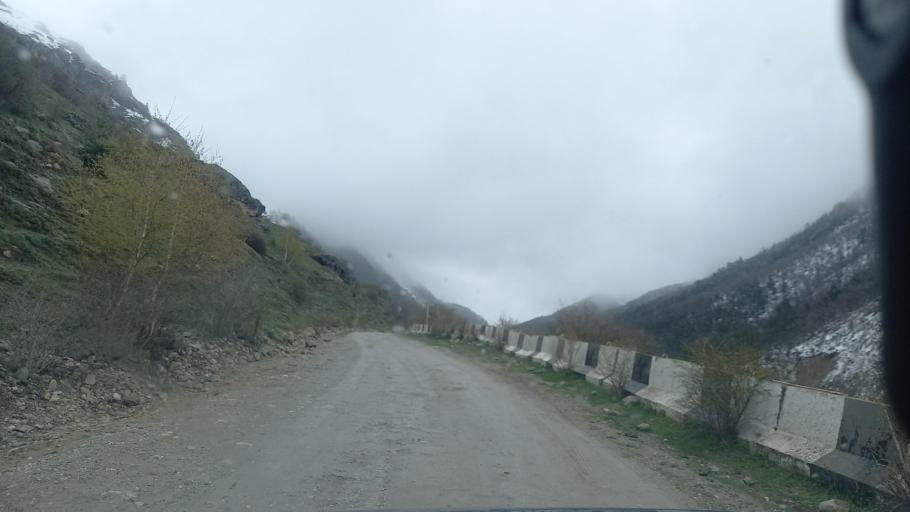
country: RU
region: Kabardino-Balkariya
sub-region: El'brusskiy Rayon
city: El'brus
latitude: 43.2271
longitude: 42.6632
